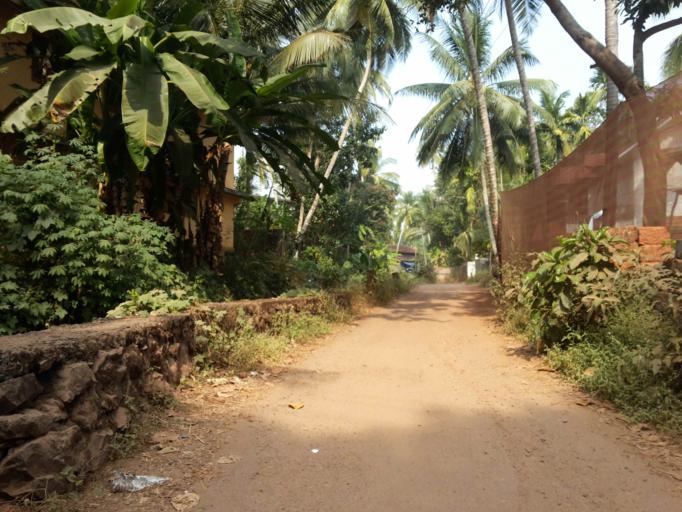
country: IN
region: Kerala
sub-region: Kozhikode
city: Kunnamangalam
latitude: 11.2963
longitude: 75.8287
